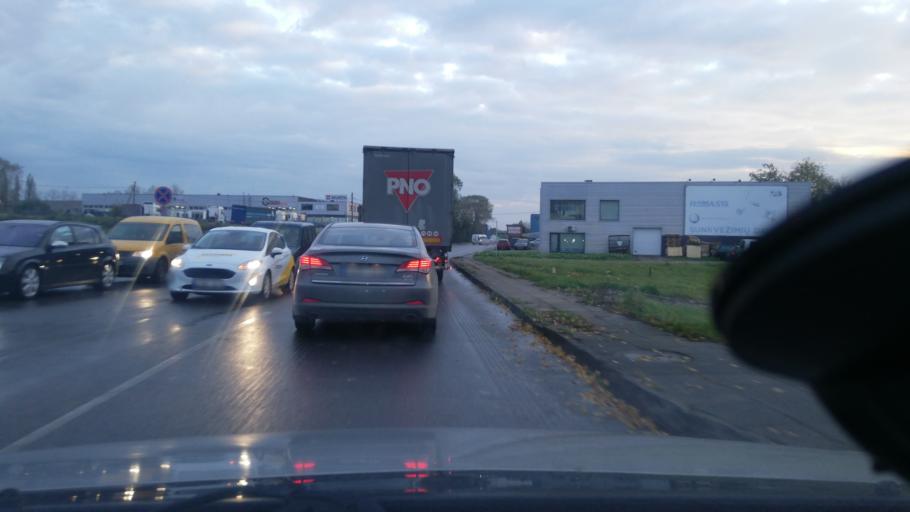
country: LT
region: Klaipedos apskritis
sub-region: Klaipeda
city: Klaipeda
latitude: 55.6859
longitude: 21.1837
